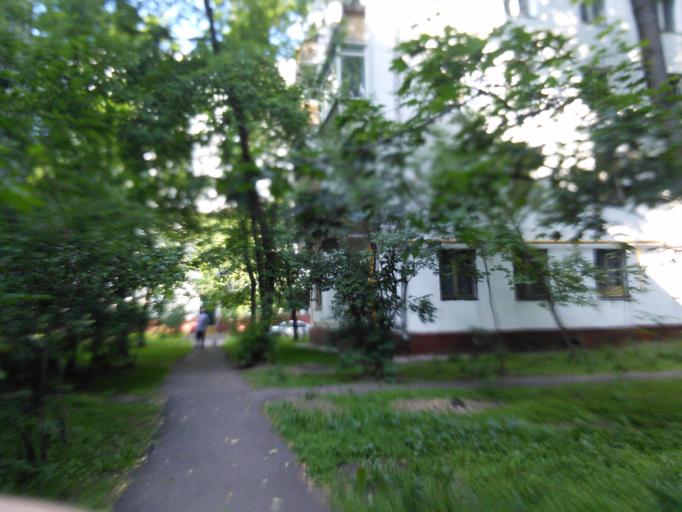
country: RU
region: Moskovskaya
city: Bogorodskoye
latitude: 55.8095
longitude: 37.7233
